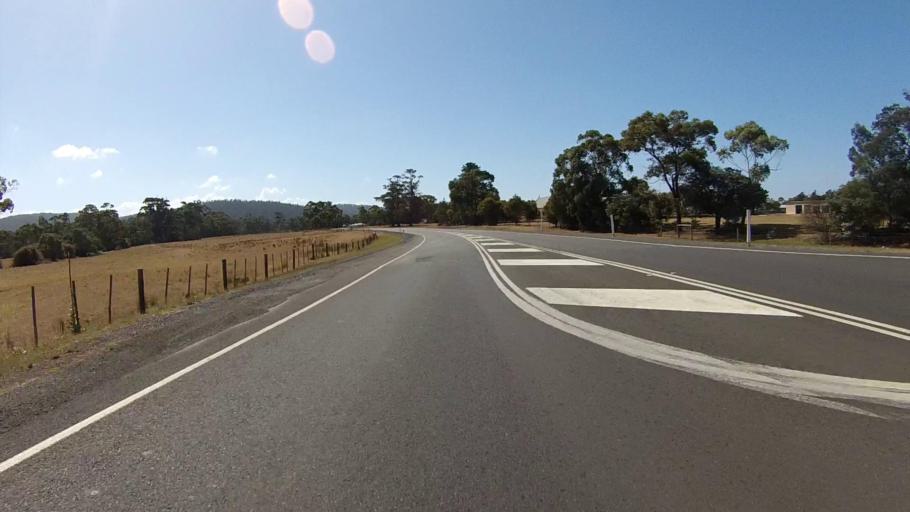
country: AU
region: Tasmania
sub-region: Sorell
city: Sorell
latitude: -42.5080
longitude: 147.9086
